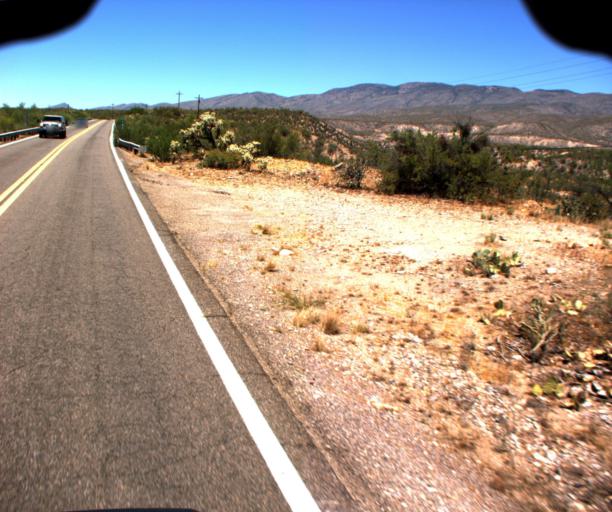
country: US
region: Arizona
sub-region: Pinal County
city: Kearny
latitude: 33.0959
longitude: -110.7303
